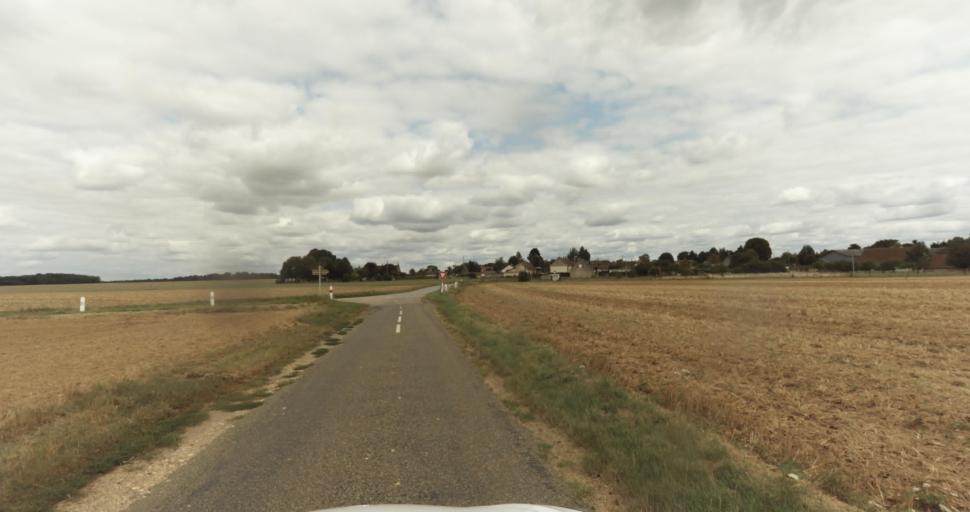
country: FR
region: Haute-Normandie
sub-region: Departement de l'Eure
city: Saint-Germain-sur-Avre
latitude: 48.8008
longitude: 1.2594
